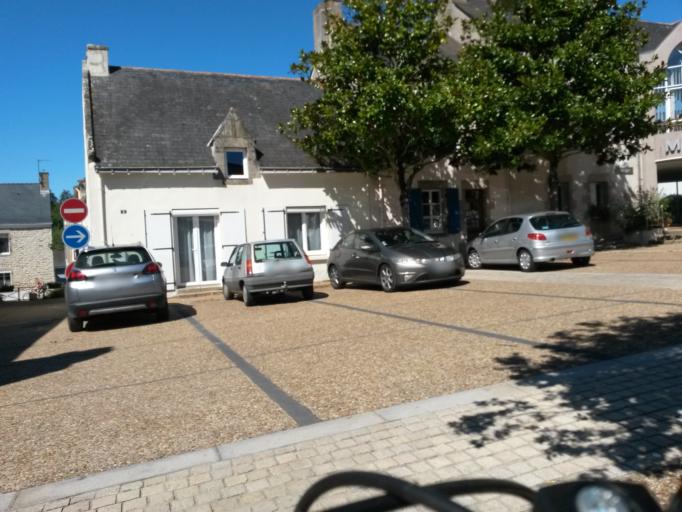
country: FR
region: Pays de la Loire
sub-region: Departement de la Loire-Atlantique
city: Mesquer
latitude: 47.3995
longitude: -2.4608
